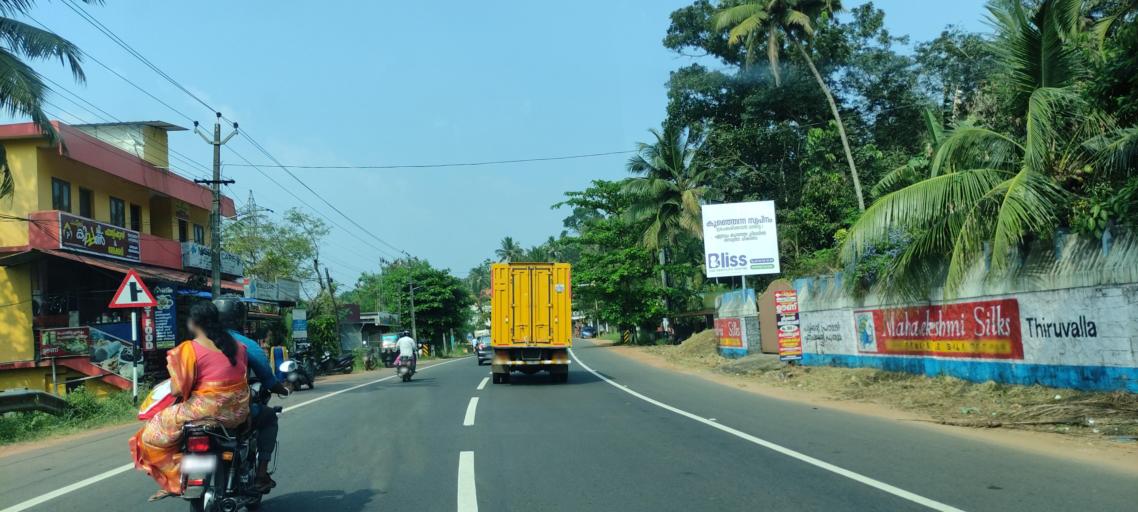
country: IN
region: Kerala
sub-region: Alappuzha
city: Chengannur
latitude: 9.2765
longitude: 76.6555
